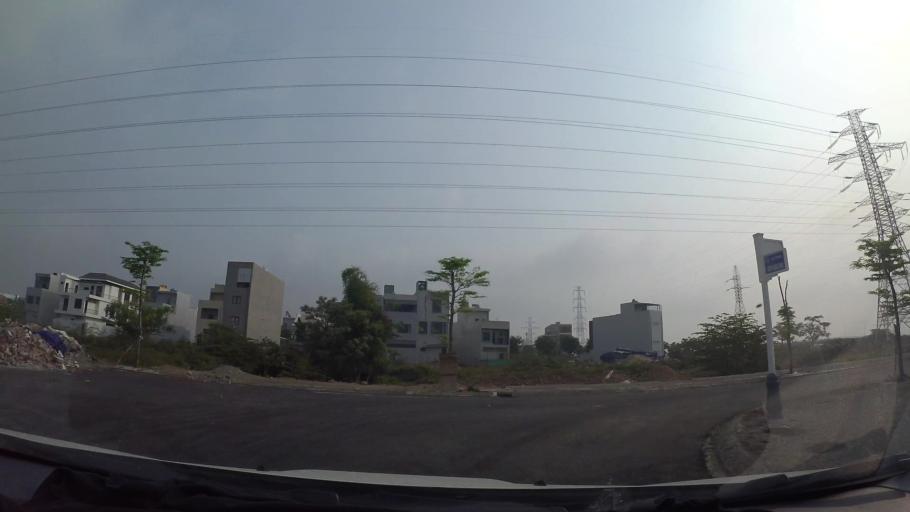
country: VN
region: Da Nang
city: Ngu Hanh Son
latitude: 16.0150
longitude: 108.2321
